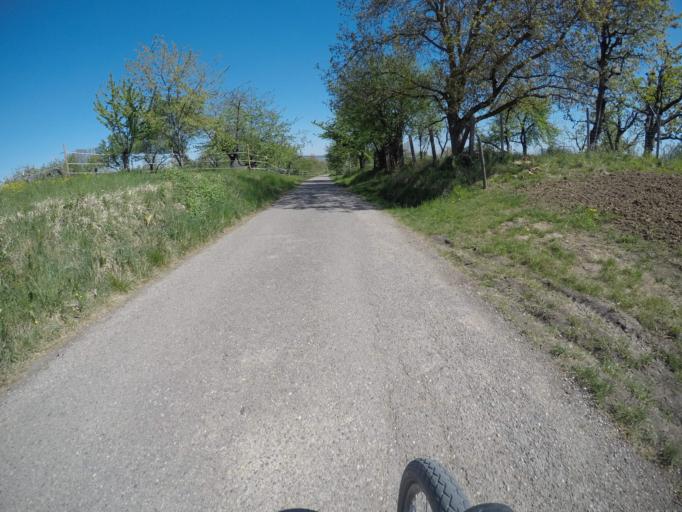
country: DE
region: Baden-Wuerttemberg
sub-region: Regierungsbezirk Stuttgart
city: Waiblingen
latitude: 48.7993
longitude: 9.3110
